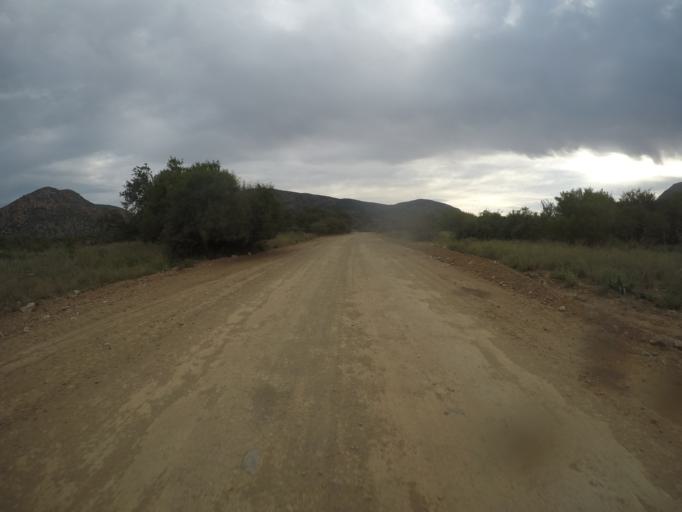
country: ZA
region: Eastern Cape
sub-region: Cacadu District Municipality
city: Willowmore
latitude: -33.5264
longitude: 23.8655
